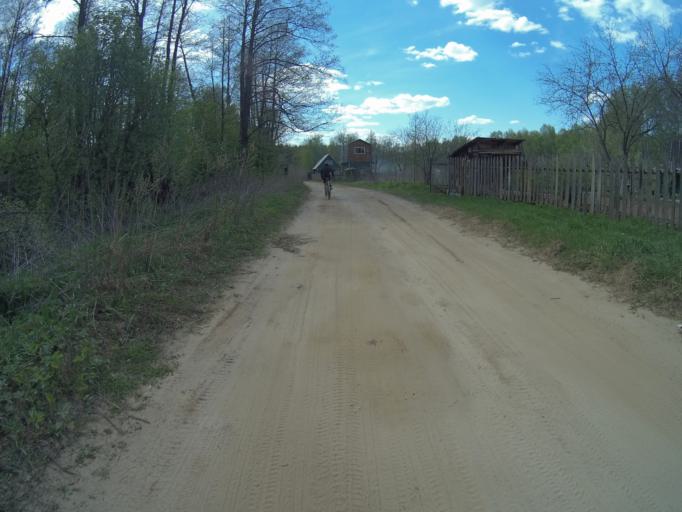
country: RU
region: Vladimir
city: Raduzhnyy
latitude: 56.0062
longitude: 40.2697
